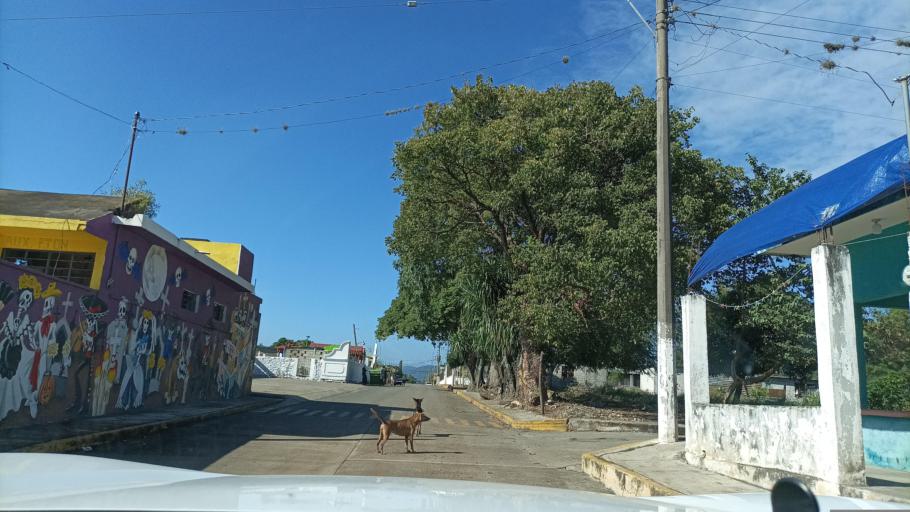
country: MX
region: Veracruz
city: Paso del Macho
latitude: 18.9675
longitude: -96.7175
